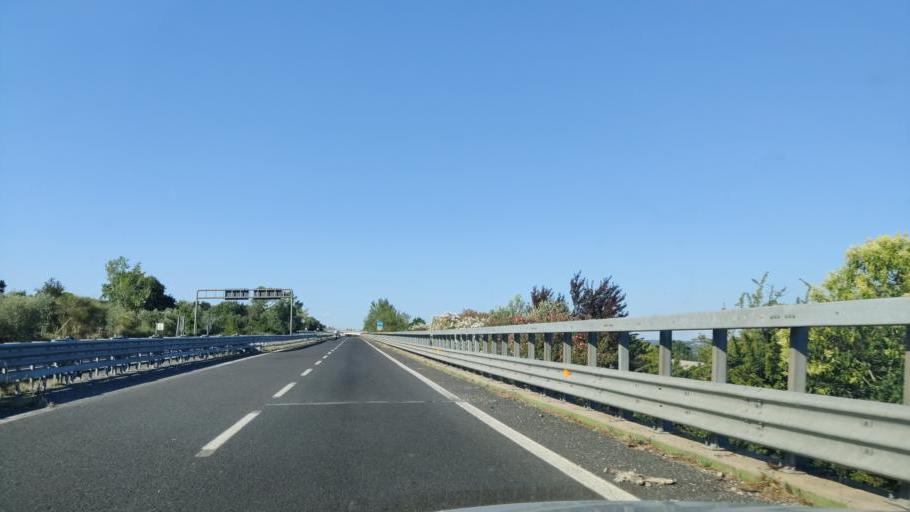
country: IT
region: Latium
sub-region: Provincia di Viterbo
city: Orte Scalo
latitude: 42.4552
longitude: 12.4065
